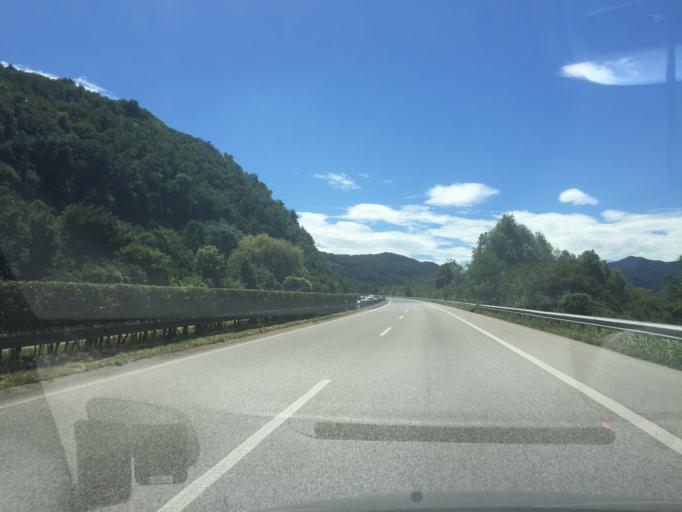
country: CH
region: Ticino
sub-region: Lugano District
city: Bioggio
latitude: 46.0092
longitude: 8.9153
